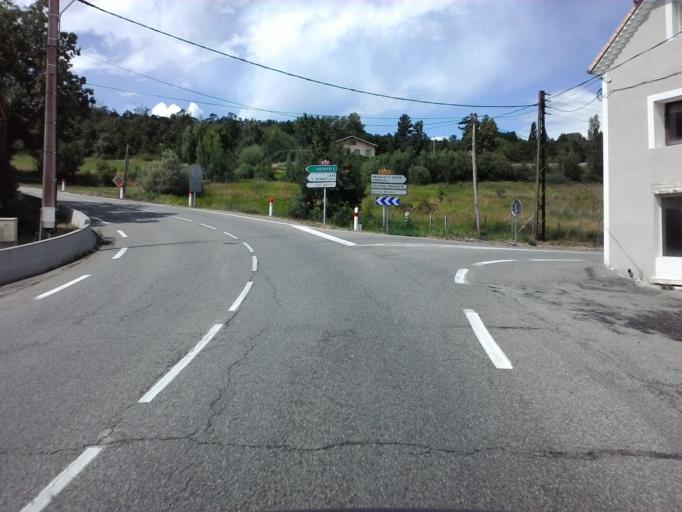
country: FR
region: Provence-Alpes-Cote d'Azur
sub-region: Departement des Hautes-Alpes
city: Gap
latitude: 44.5889
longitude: 6.0812
